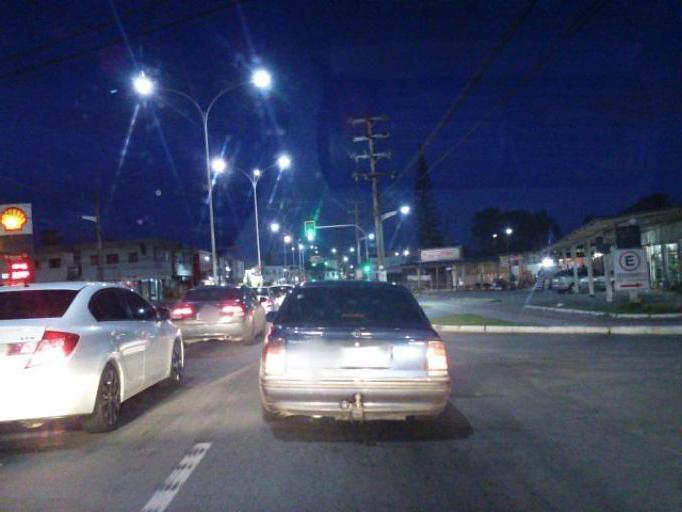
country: BR
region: Santa Catarina
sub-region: Itajai
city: Itajai
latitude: -26.8848
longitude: -48.6959
